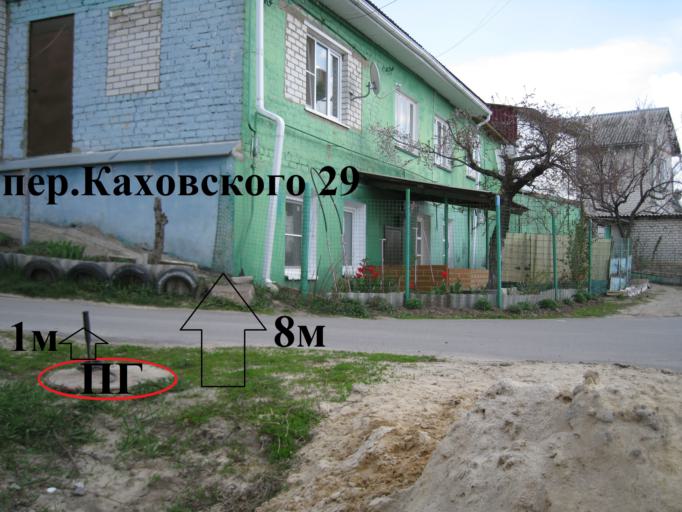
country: RU
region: Voronezj
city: Voronezh
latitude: 51.6464
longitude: 39.1912
